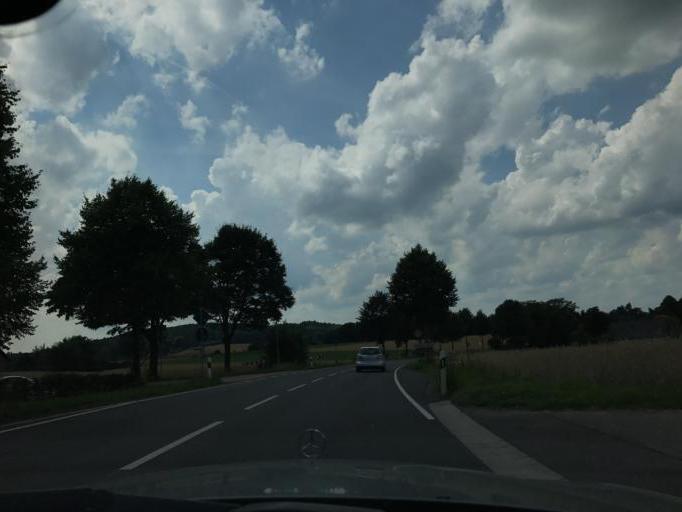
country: DE
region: Lower Saxony
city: Hagen
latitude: 52.1960
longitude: 7.9607
